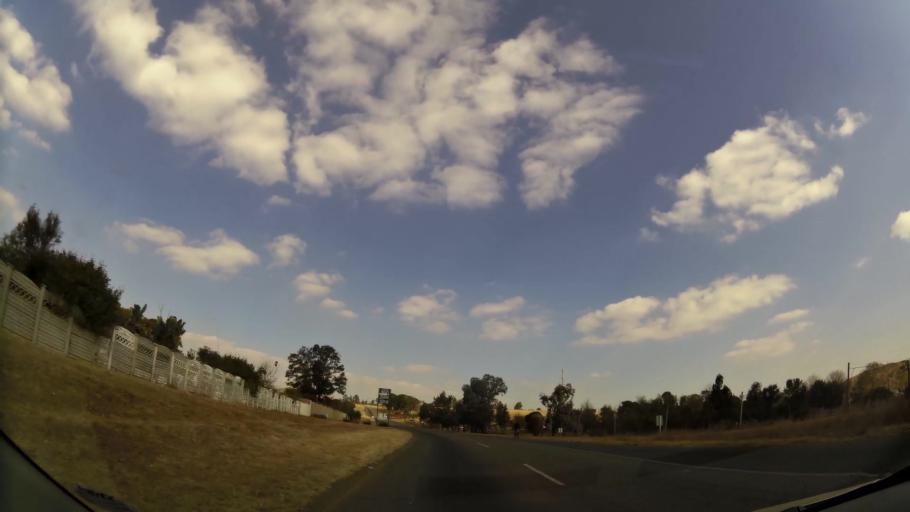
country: ZA
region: Gauteng
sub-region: West Rand District Municipality
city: Krugersdorp
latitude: -26.0510
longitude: 27.7540
